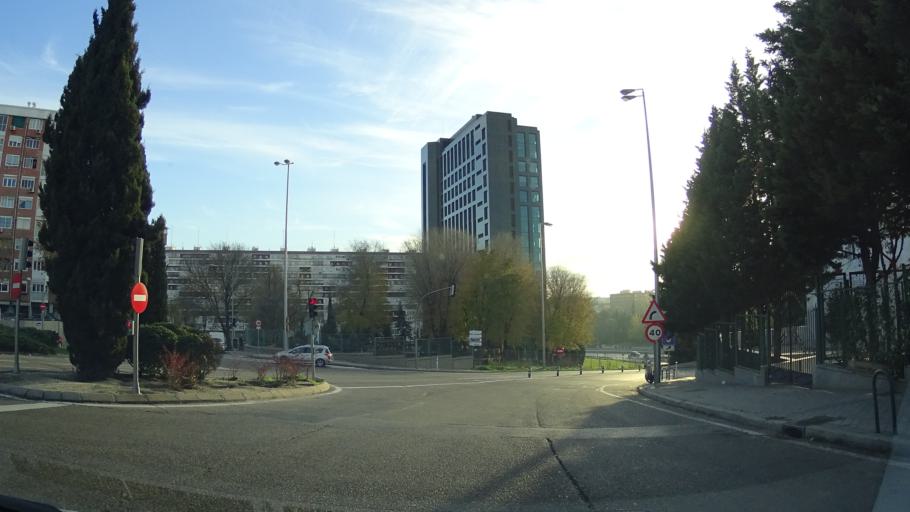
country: ES
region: Madrid
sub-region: Provincia de Madrid
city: Ciudad Lineal
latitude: 40.4383
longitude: -3.6573
